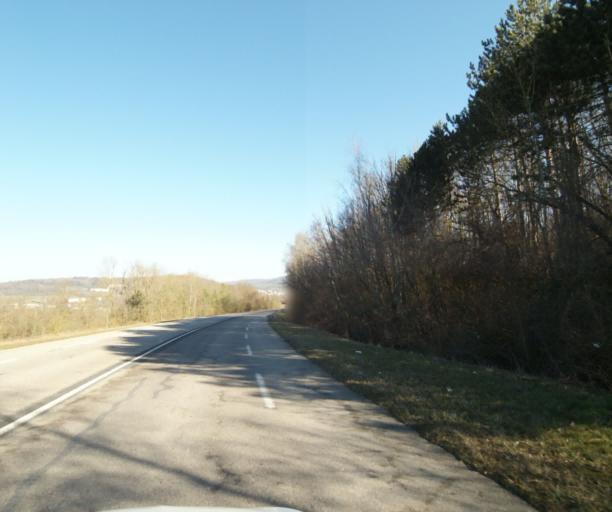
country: FR
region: Lorraine
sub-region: Departement de Meurthe-et-Moselle
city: Champigneulles
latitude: 48.7361
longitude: 6.1824
